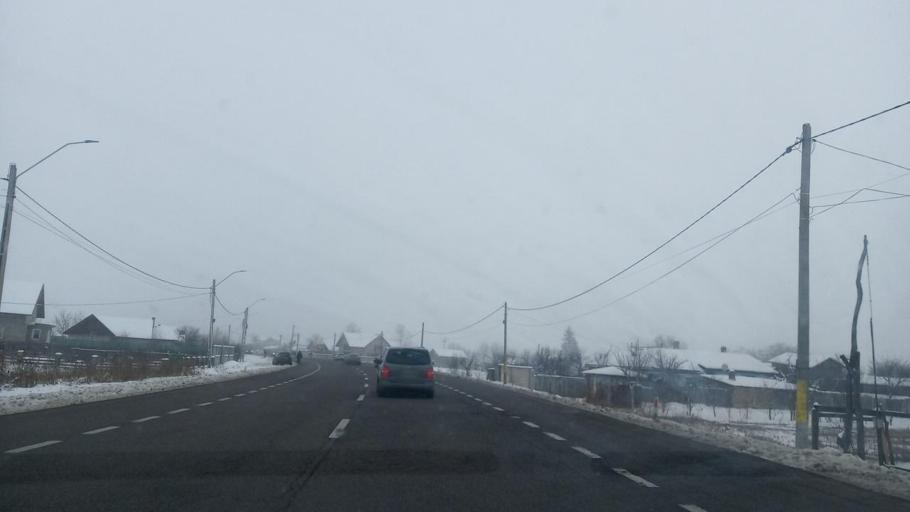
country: RO
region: Bacau
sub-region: Comuna Filipesti
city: Filipesti
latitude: 46.7819
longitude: 26.8910
